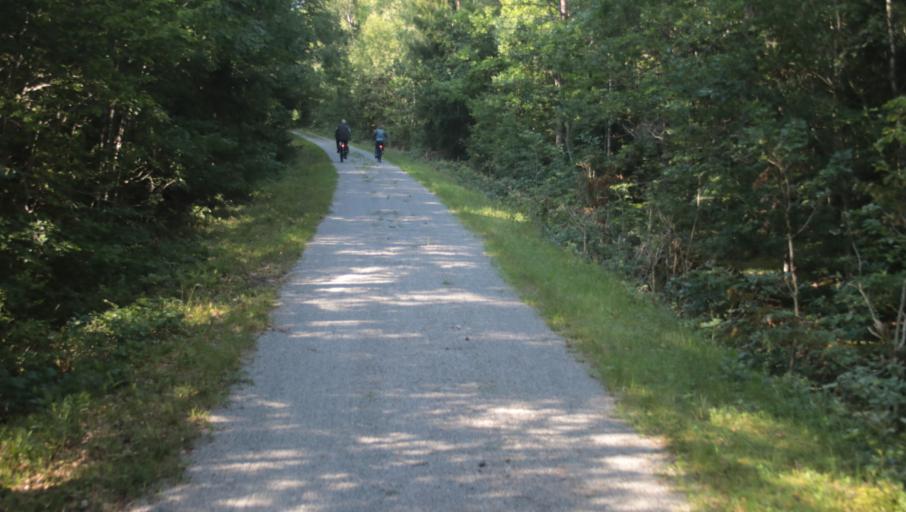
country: SE
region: Blekinge
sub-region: Karlshamns Kommun
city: Svangsta
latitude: 56.3353
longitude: 14.6992
